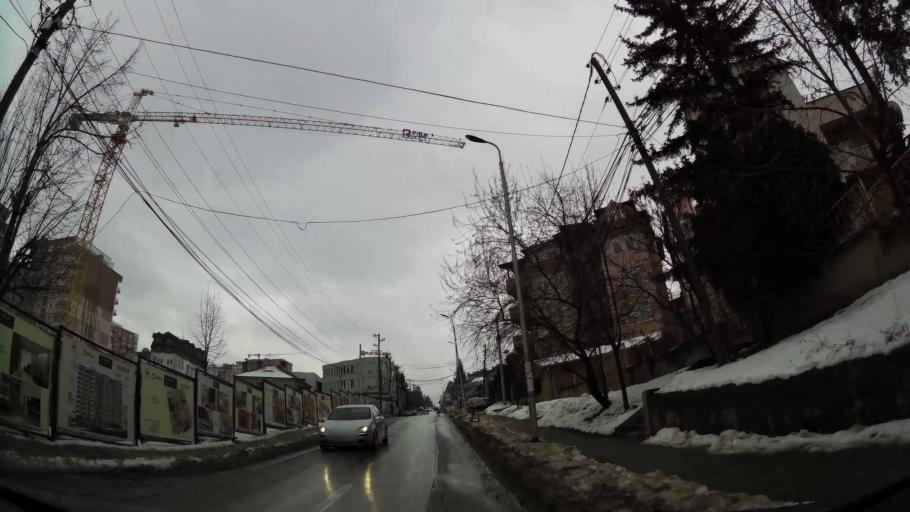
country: XK
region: Pristina
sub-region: Komuna e Prishtines
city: Pristina
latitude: 42.6566
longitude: 21.1681
